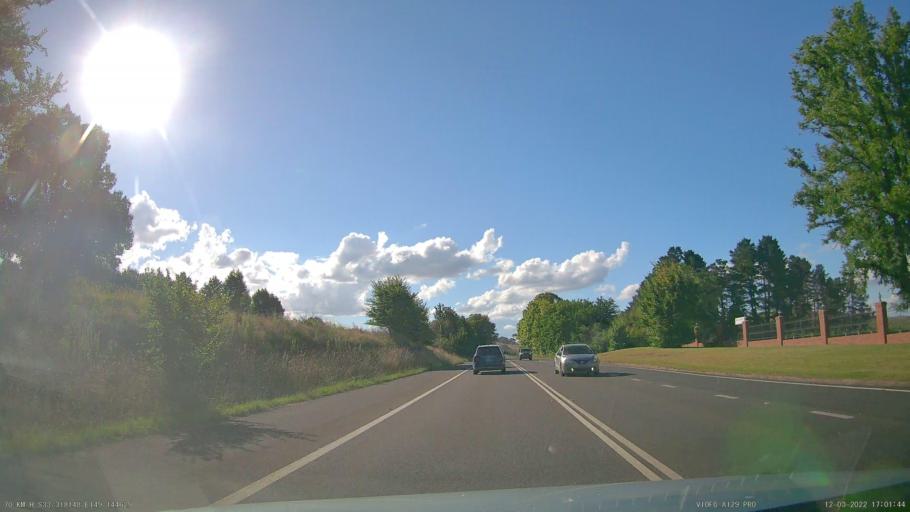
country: AU
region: New South Wales
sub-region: Orange Municipality
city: Orange
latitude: -33.3180
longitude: 149.1445
